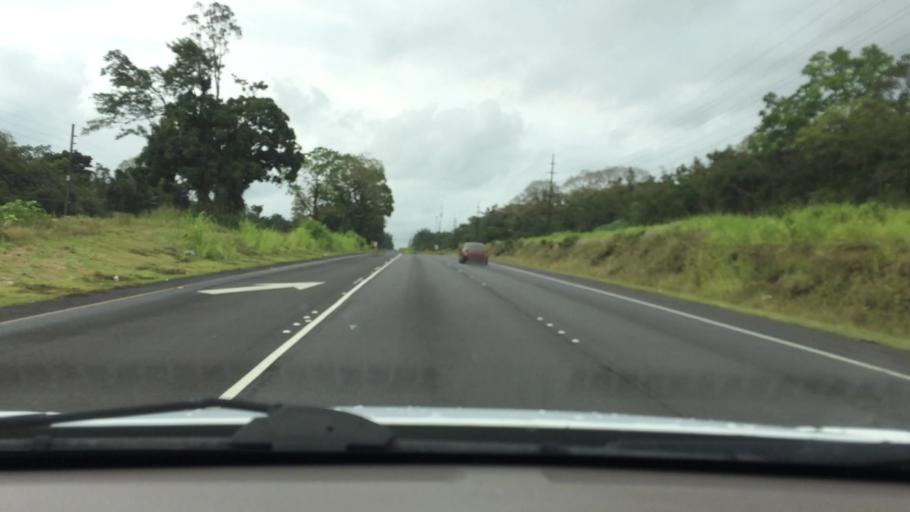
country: US
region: Hawaii
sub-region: Hawaii County
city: Kea'au
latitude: 19.6503
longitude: -155.0518
